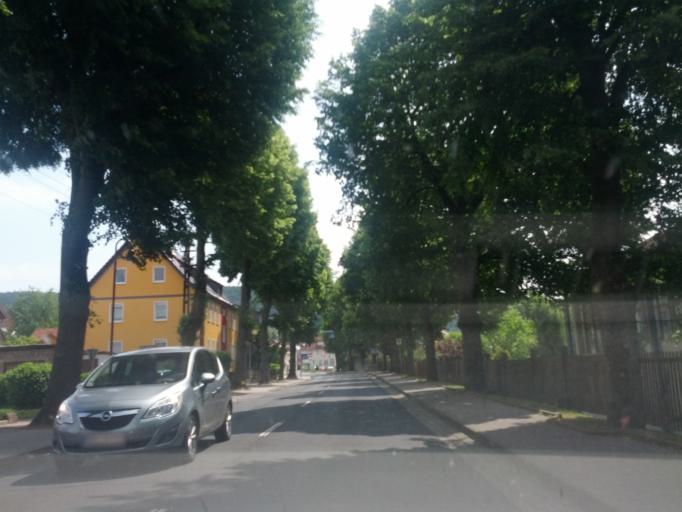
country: DE
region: Thuringia
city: Stadtlengsfeld
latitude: 50.7840
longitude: 10.1253
